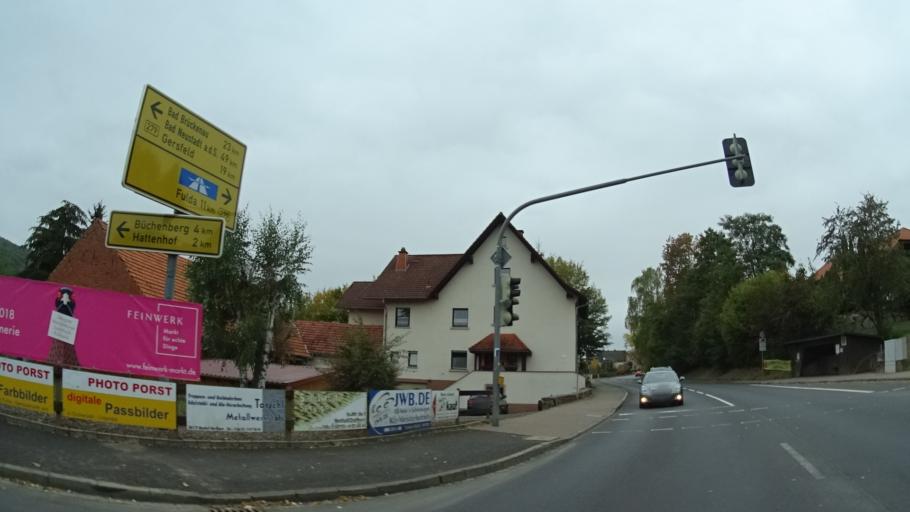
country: DE
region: Hesse
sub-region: Regierungsbezirk Kassel
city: Eichenzell
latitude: 50.4669
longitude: 9.7063
